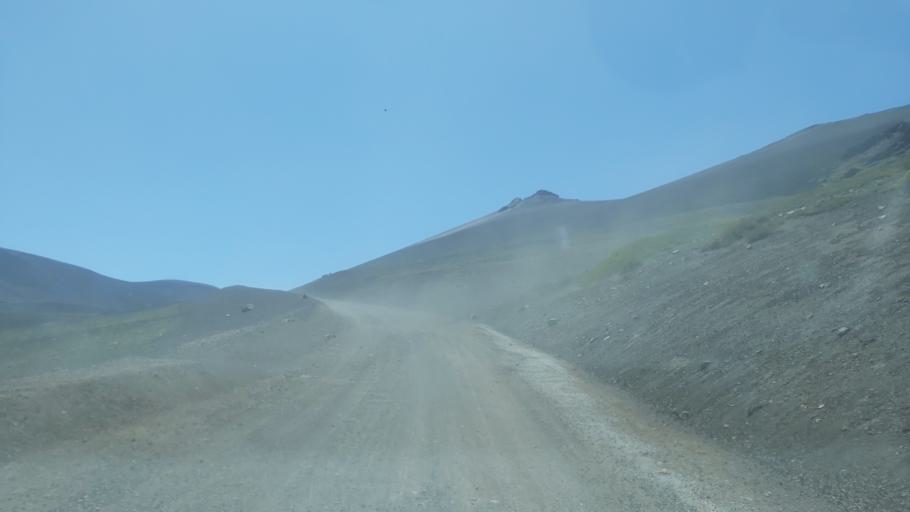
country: CL
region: Araucania
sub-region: Provincia de Cautin
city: Vilcun
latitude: -38.4123
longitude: -71.5419
